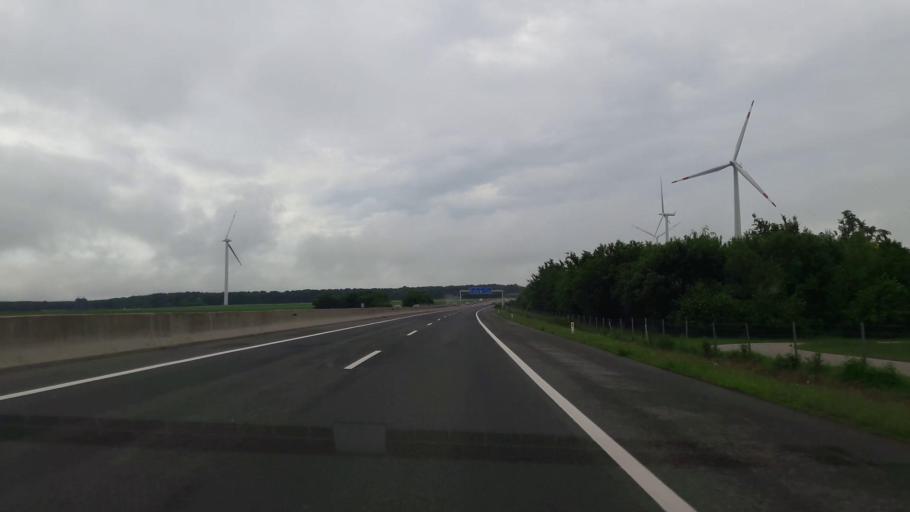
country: AT
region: Burgenland
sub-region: Politischer Bezirk Mattersburg
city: Pottelsdorf
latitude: 47.7675
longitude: 16.4251
